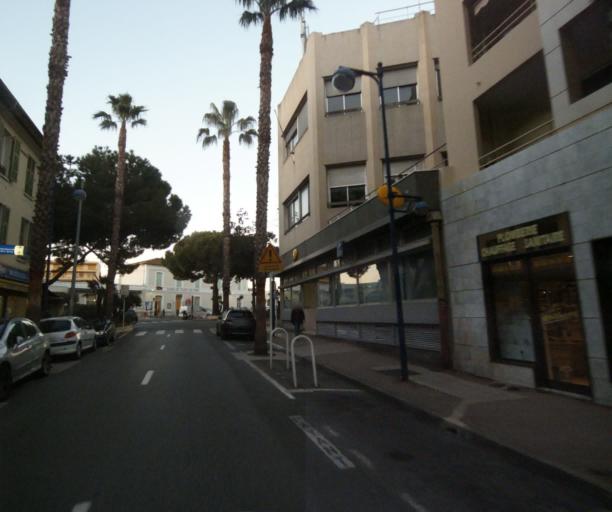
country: FR
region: Provence-Alpes-Cote d'Azur
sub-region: Departement des Alpes-Maritimes
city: Antibes
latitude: 43.5703
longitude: 7.1113
